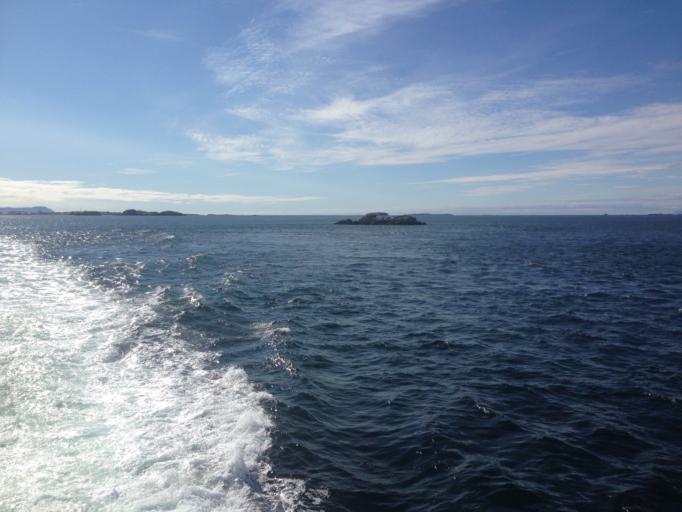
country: IS
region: West
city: Stykkisholmur
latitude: 65.0903
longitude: -22.6221
